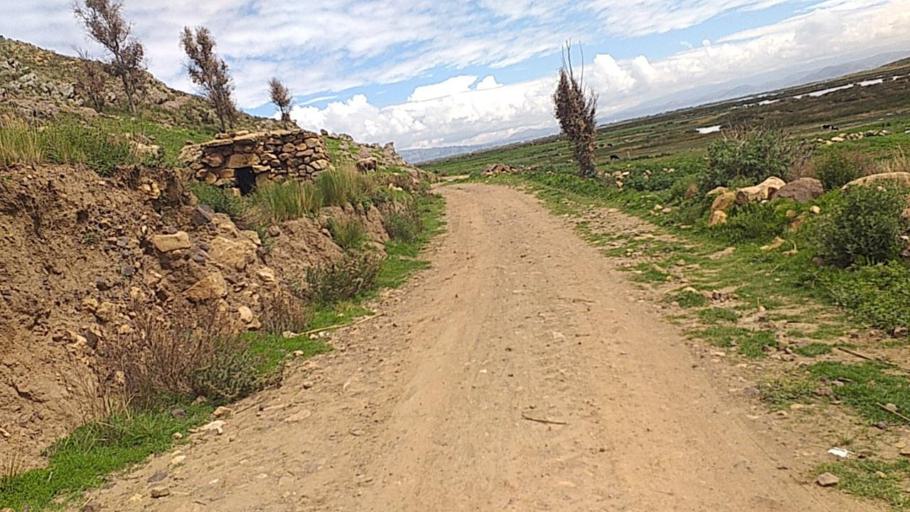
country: BO
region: La Paz
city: Batallas
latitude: -16.3394
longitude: -68.6360
